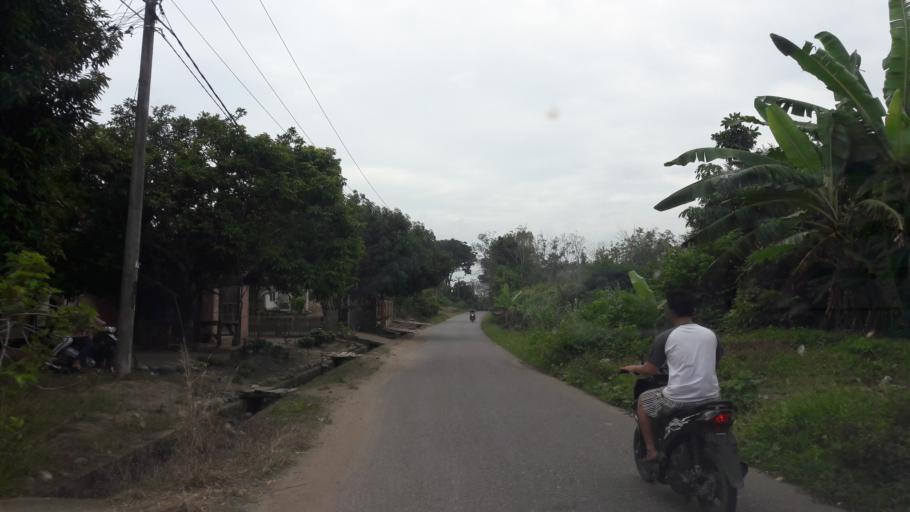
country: ID
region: South Sumatra
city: Gunungmenang
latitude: -3.1447
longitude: 104.1143
